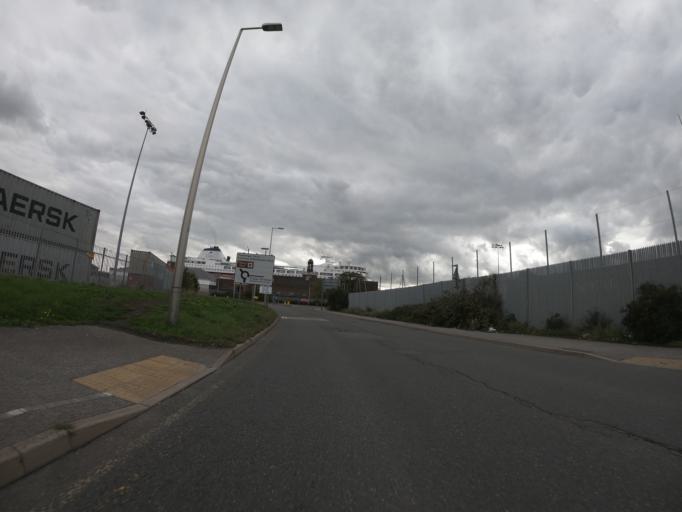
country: GB
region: England
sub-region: Borough of Thurrock
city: Tilbury
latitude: 51.4527
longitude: 0.3637
